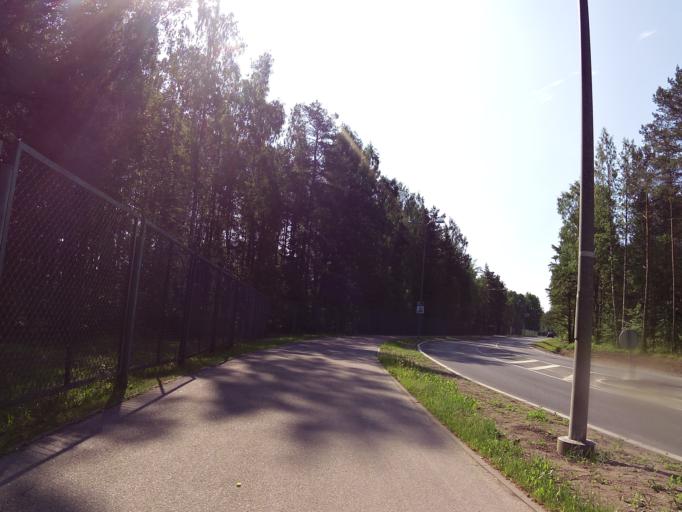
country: EE
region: Harju
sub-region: Saue vald
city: Laagri
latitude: 59.4384
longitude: 24.6264
